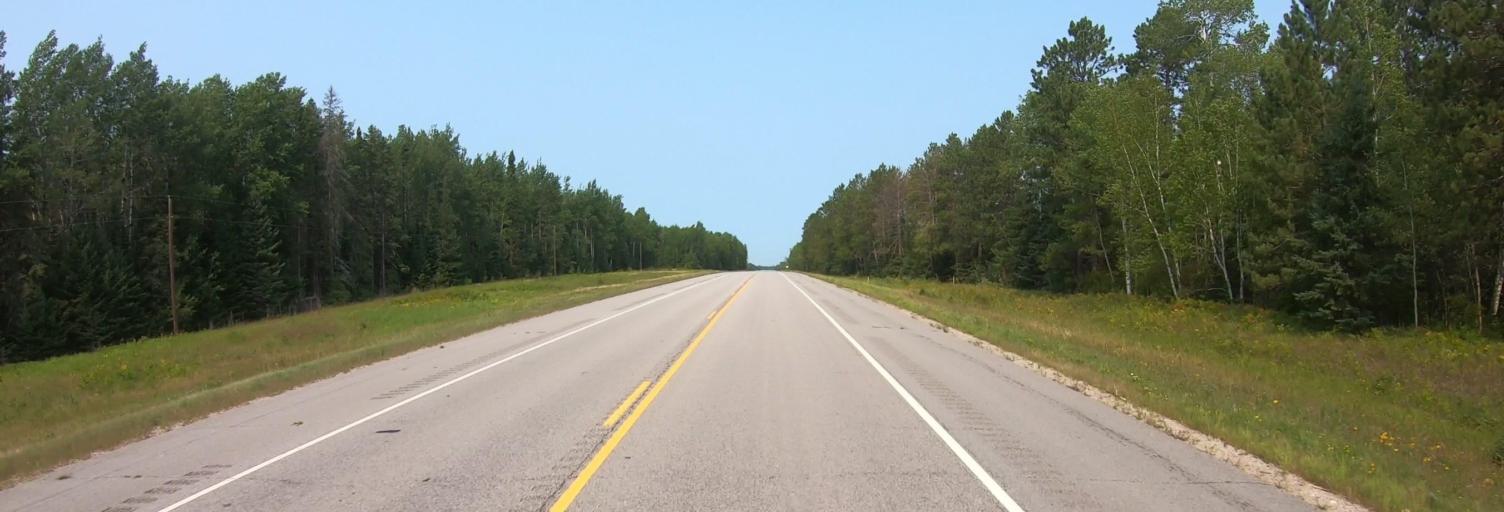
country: CA
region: Ontario
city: Fort Frances
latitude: 48.3768
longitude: -92.9817
